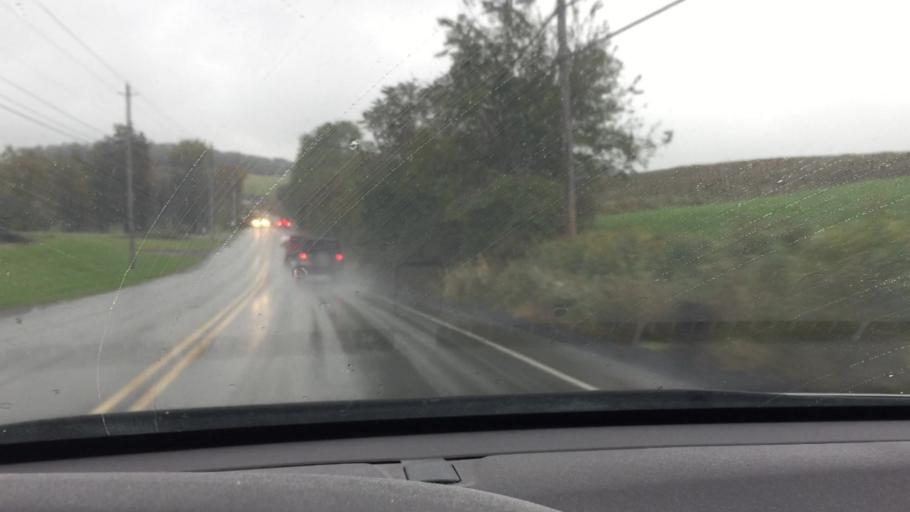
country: US
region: Pennsylvania
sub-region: Westmoreland County
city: Fellsburg
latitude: 40.1651
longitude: -79.8185
